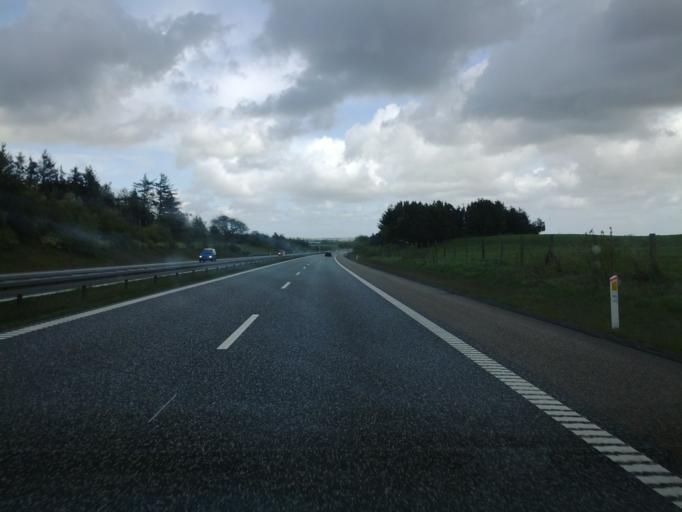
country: DK
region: North Denmark
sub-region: Bronderslev Kommune
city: Dronninglund
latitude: 57.2363
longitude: 10.2550
